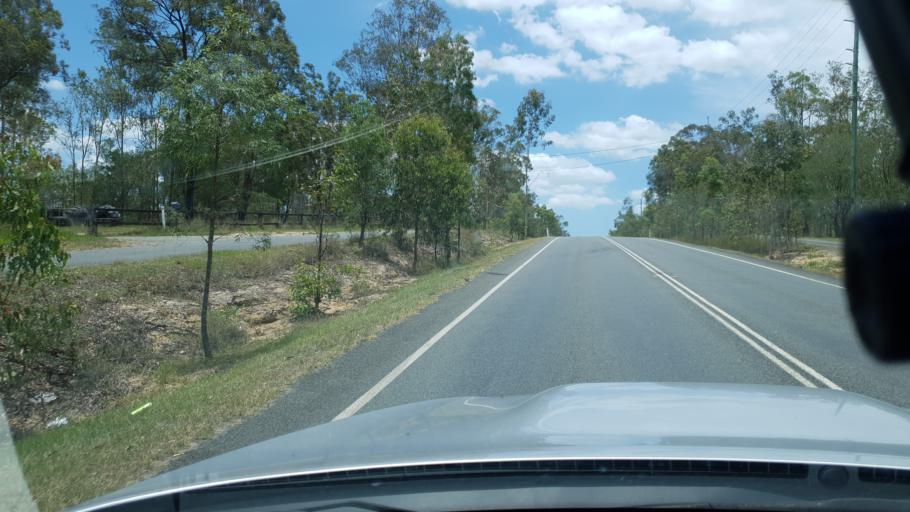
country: AU
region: Queensland
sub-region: Logan
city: North Maclean
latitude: -27.8155
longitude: 152.9735
